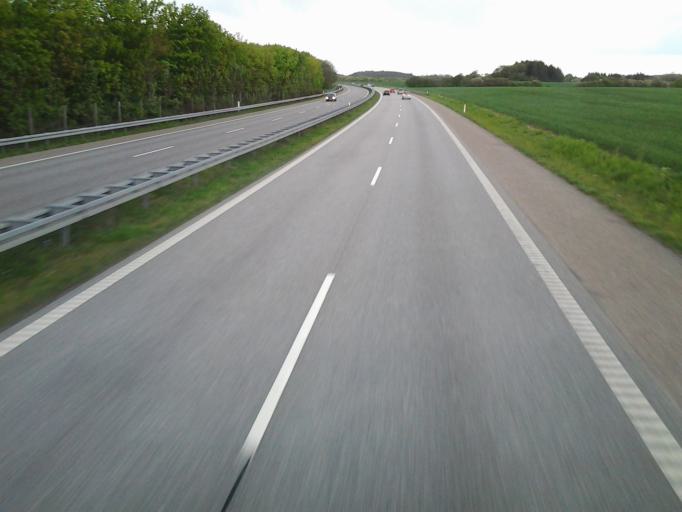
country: DK
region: Zealand
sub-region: Faxe Kommune
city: Ronnede
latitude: 55.1972
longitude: 11.9755
